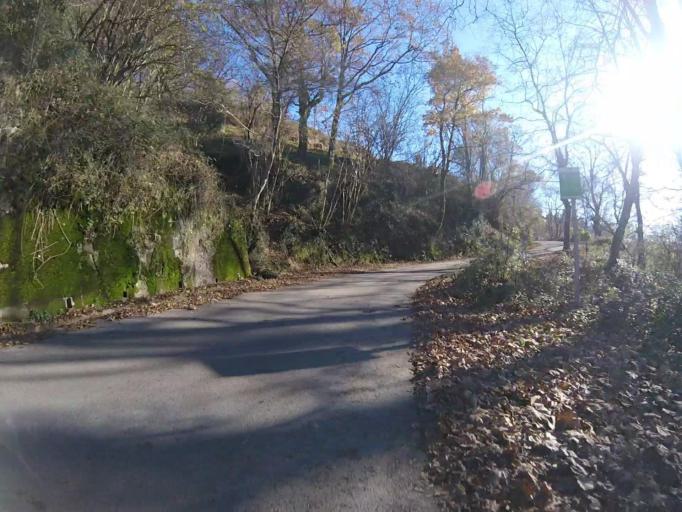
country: ES
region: Navarre
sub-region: Provincia de Navarra
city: Bera
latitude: 43.3091
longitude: -1.6829
